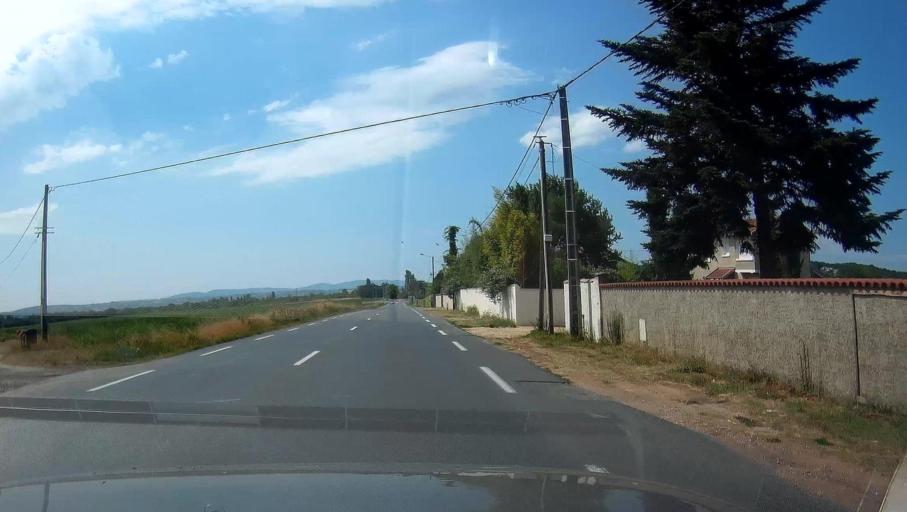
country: FR
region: Rhone-Alpes
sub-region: Departement de l'Ain
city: Reyrieux
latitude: 45.9300
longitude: 4.8051
